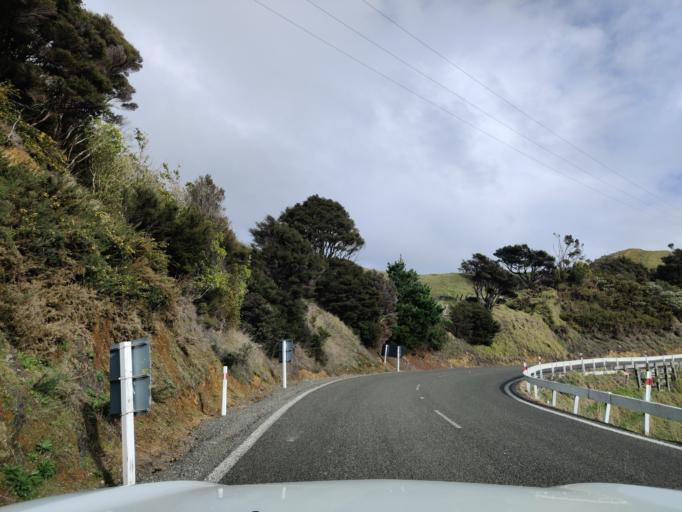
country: NZ
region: Waikato
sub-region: Thames-Coromandel District
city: Coromandel
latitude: -36.8153
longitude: 175.4867
